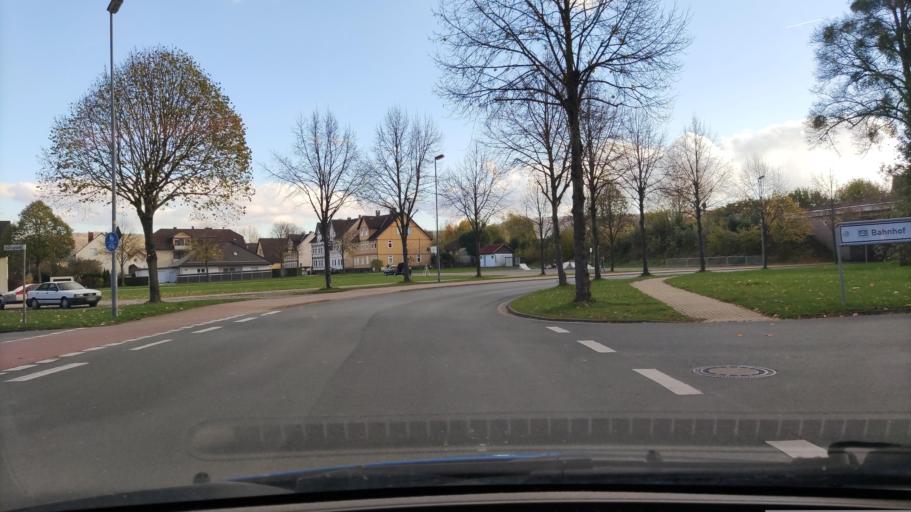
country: DE
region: Lower Saxony
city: Stadtoldendorf
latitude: 51.8806
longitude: 9.6228
